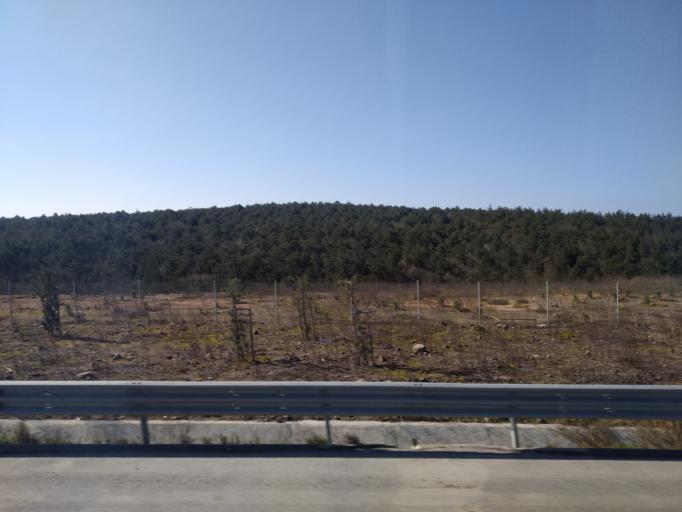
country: TR
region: Istanbul
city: Sancaktepe
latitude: 41.0570
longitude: 29.2758
